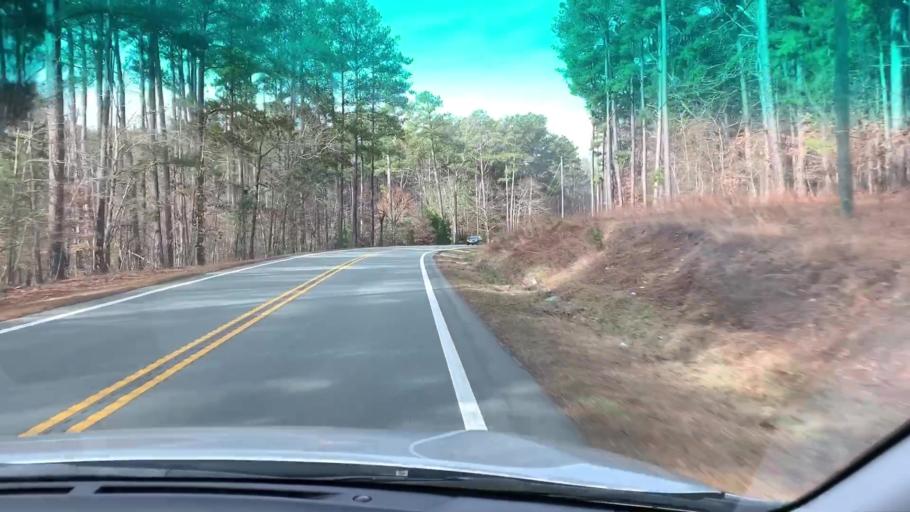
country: US
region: North Carolina
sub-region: Wake County
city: Green Level
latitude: 35.8469
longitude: -78.9298
